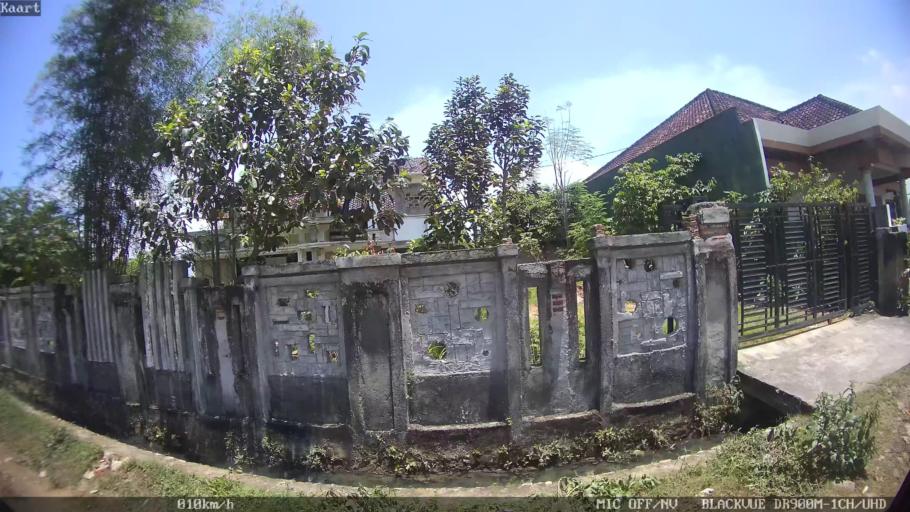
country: ID
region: Lampung
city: Kedaton
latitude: -5.3732
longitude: 105.2871
